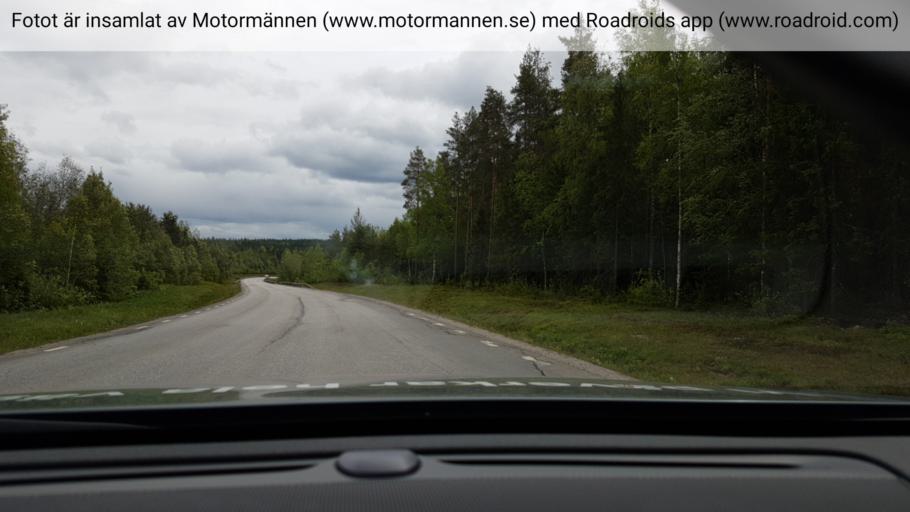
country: SE
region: Vaesterbotten
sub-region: Vannas Kommun
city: Vaennaes
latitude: 63.9473
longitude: 19.7605
